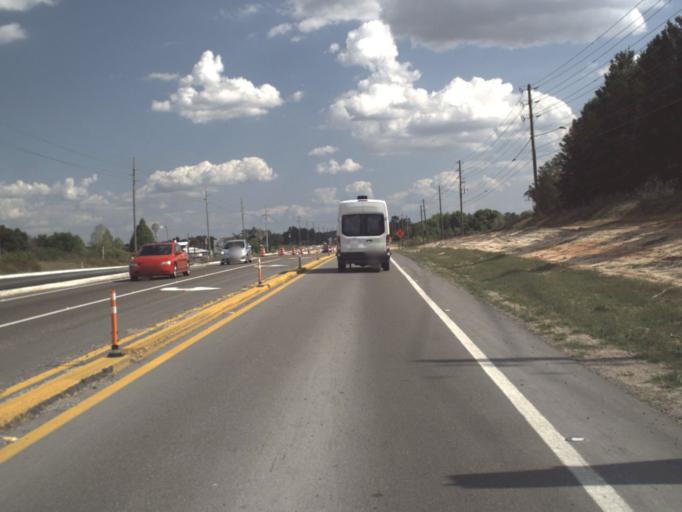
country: US
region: Florida
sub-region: Lake County
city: Four Corners
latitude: 28.4225
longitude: -81.7081
